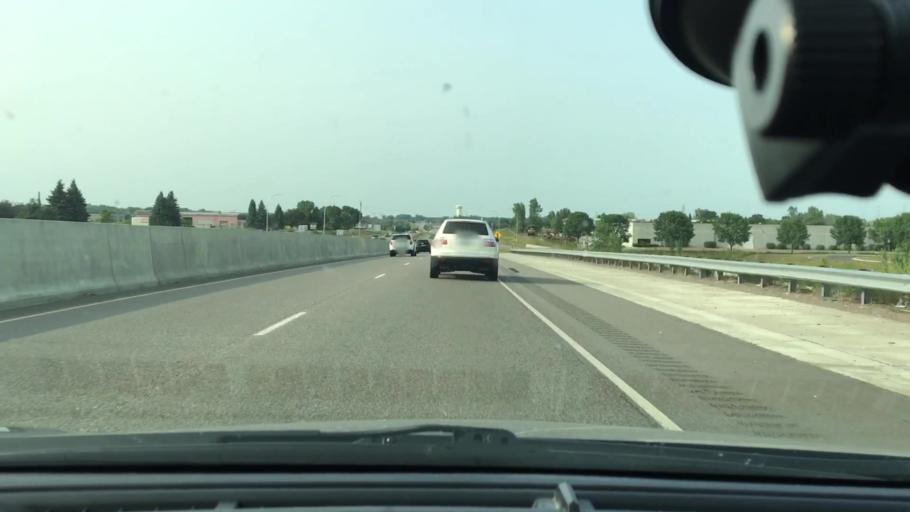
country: US
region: Minnesota
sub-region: Hennepin County
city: Rogers
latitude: 45.2115
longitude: -93.5525
